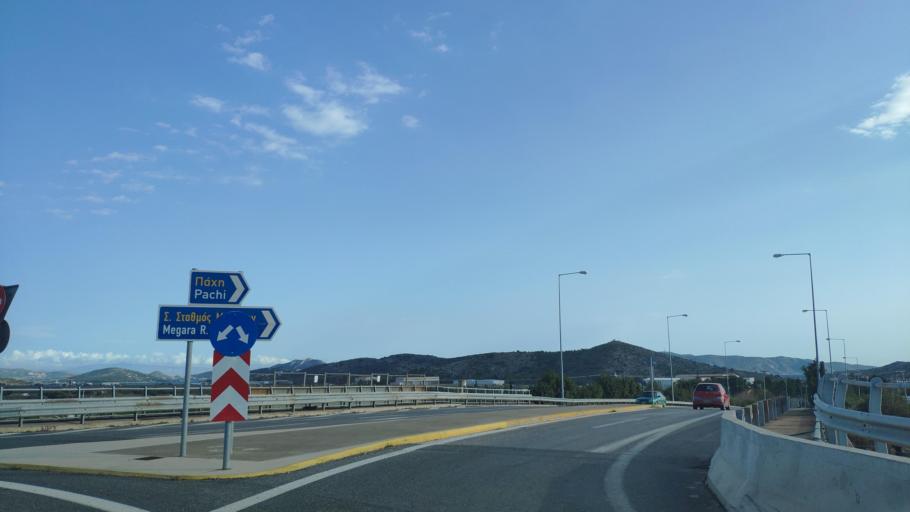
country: GR
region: Attica
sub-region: Nomarchia Dytikis Attikis
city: Megara
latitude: 37.9853
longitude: 23.3516
